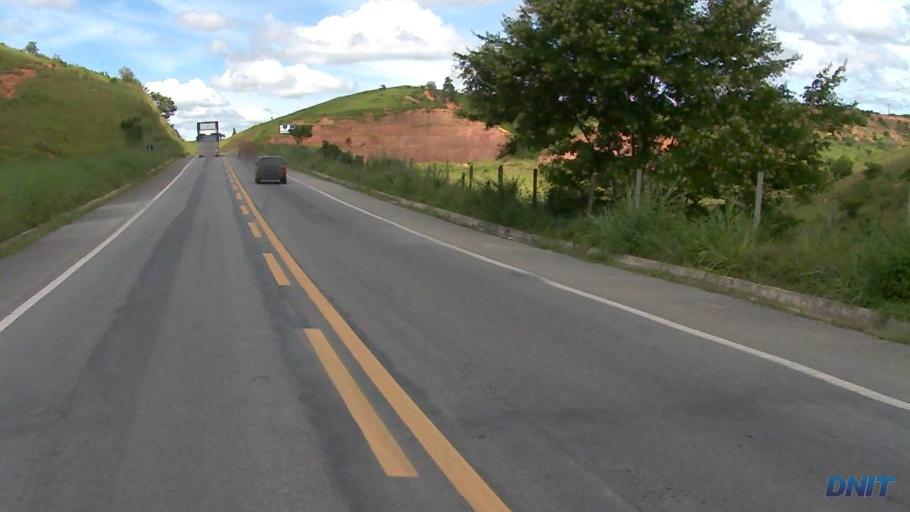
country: BR
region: Minas Gerais
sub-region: Governador Valadares
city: Governador Valadares
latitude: -19.0304
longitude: -42.1490
